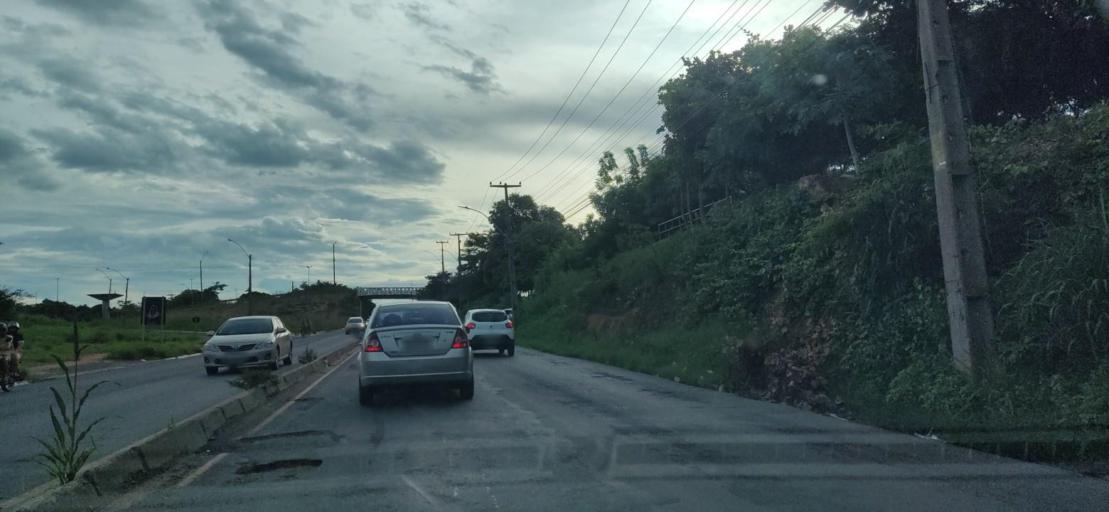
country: BR
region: Piaui
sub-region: Teresina
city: Teresina
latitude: -5.1164
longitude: -42.7818
